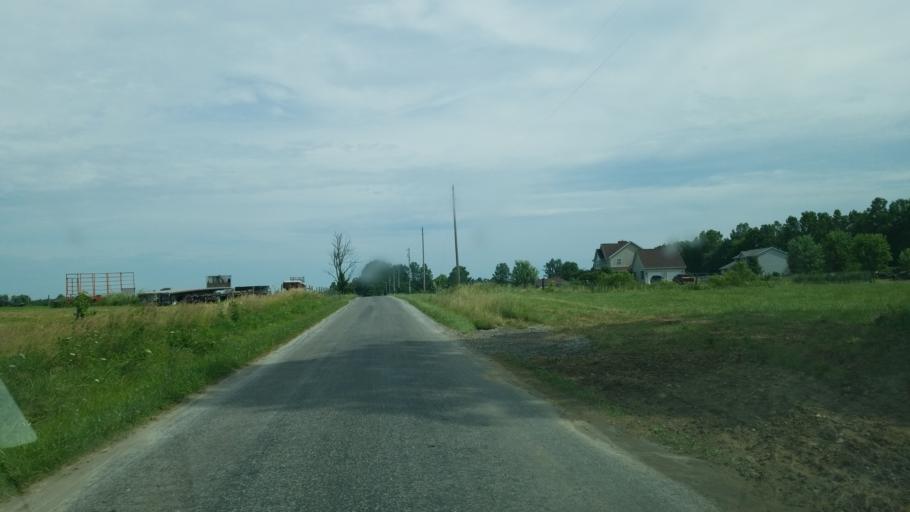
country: US
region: Ohio
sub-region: Ashland County
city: Ashland
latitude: 40.9093
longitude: -82.4069
